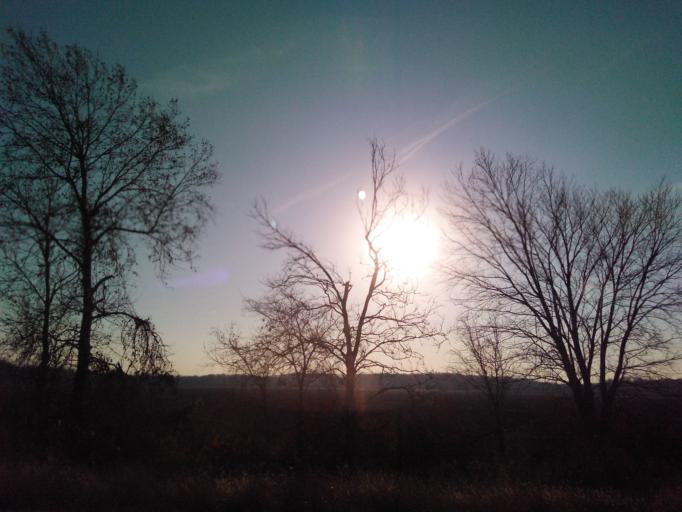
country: US
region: Illinois
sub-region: Saint Clair County
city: Caseyville
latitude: 38.6524
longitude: -90.0341
